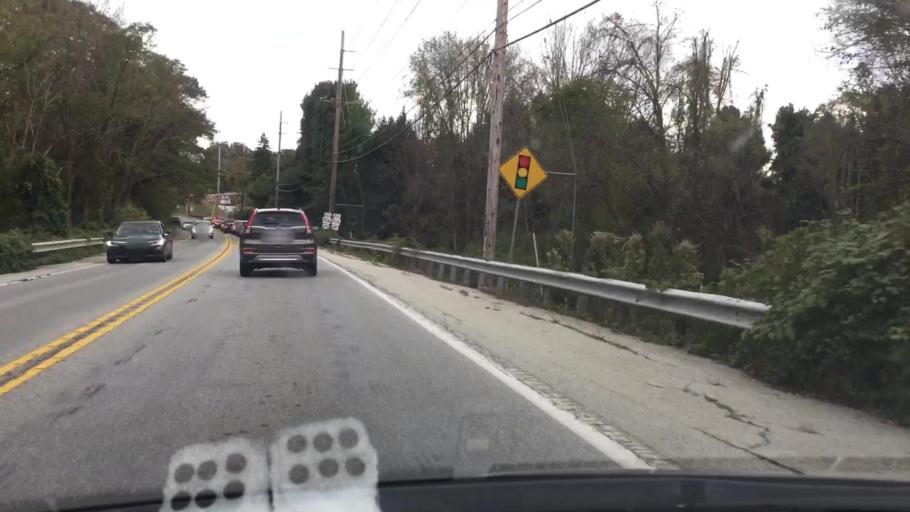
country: US
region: Pennsylvania
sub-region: Delaware County
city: Chester Heights
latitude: 39.9520
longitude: -75.5122
